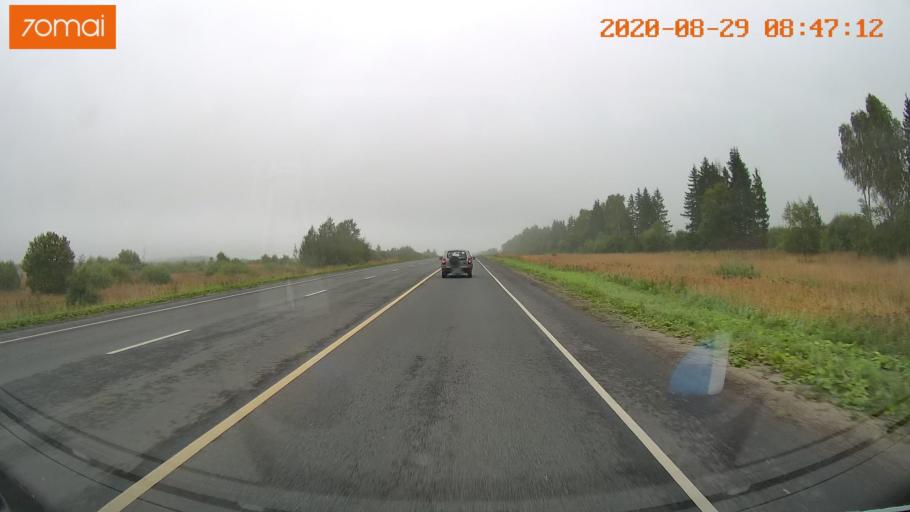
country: RU
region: Ivanovo
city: Rodniki
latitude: 57.1477
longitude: 41.8283
